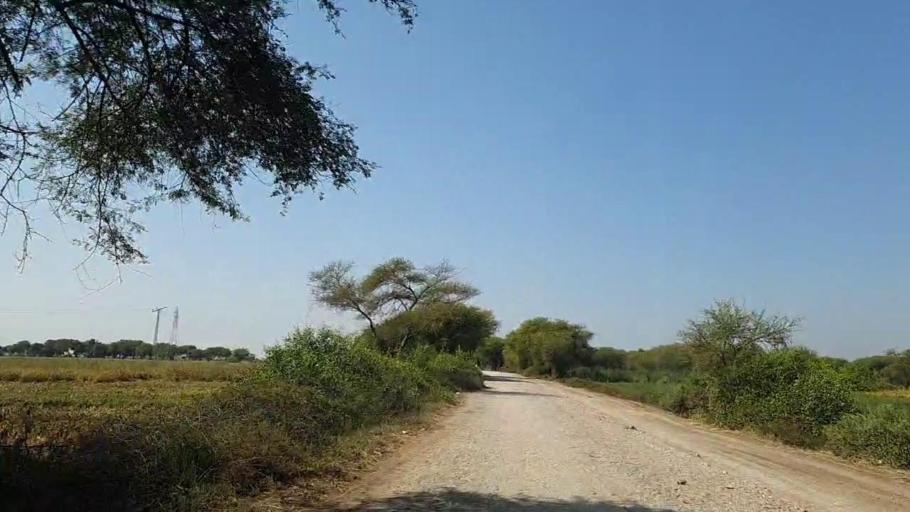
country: PK
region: Sindh
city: Chuhar Jamali
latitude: 24.4171
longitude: 68.0287
